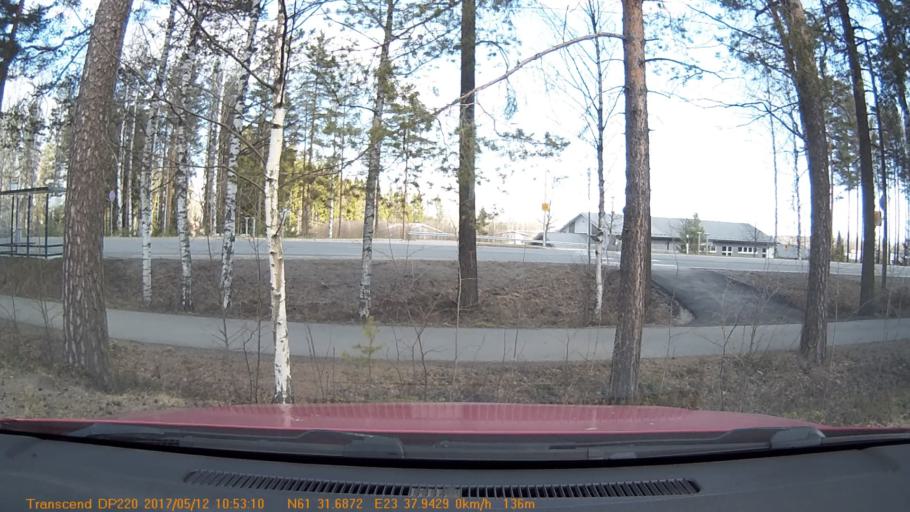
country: FI
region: Pirkanmaa
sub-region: Tampere
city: Yloejaervi
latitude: 61.5281
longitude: 23.6324
